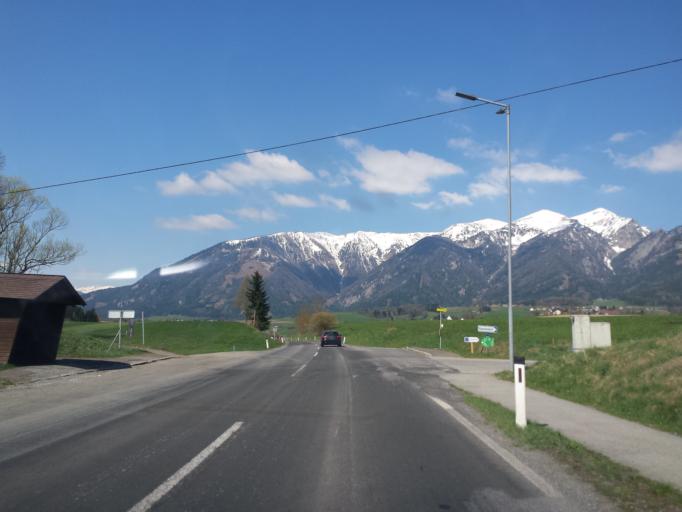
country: AT
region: Styria
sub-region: Politischer Bezirk Leoben
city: Trofaiach
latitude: 47.4071
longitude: 14.9849
